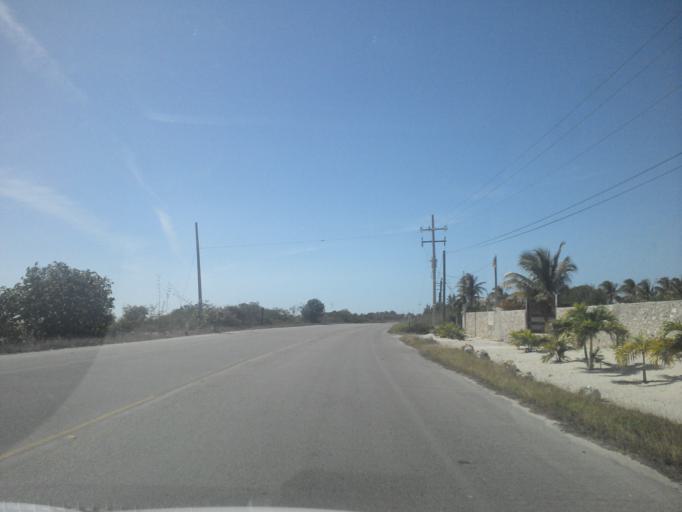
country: MX
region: Yucatan
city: Telchac Puerto
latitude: 21.3315
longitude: -89.3616
